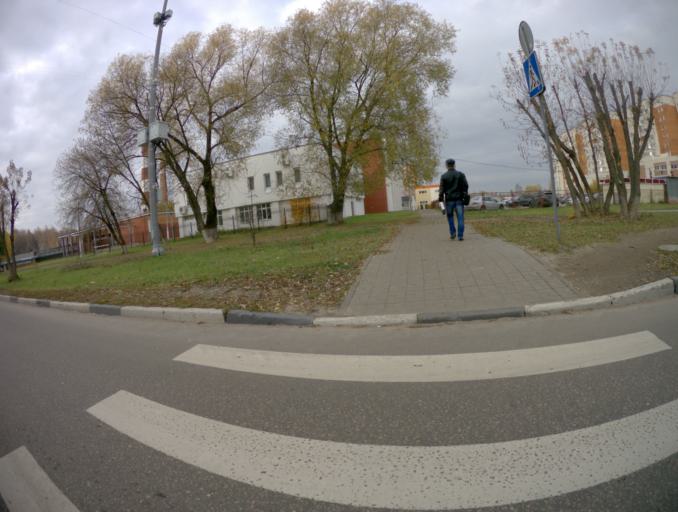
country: RU
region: Moskovskaya
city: Orekhovo-Zuyevo
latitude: 55.8077
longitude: 38.9574
